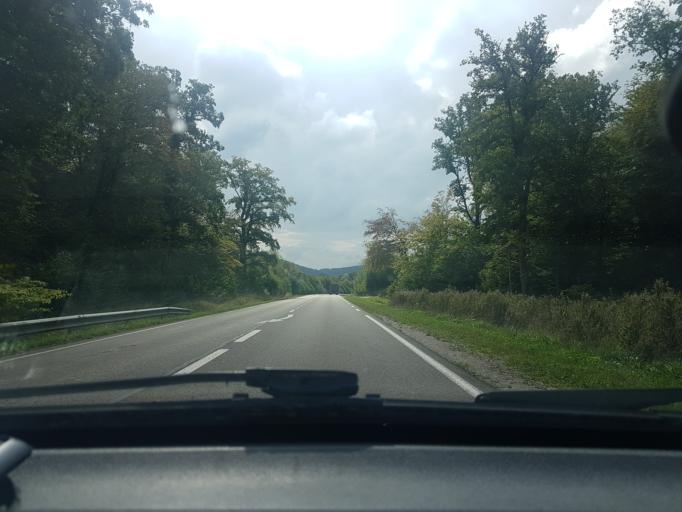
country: FR
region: Franche-Comte
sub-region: Departement de la Haute-Saone
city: Hericourt
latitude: 47.5957
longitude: 6.7200
